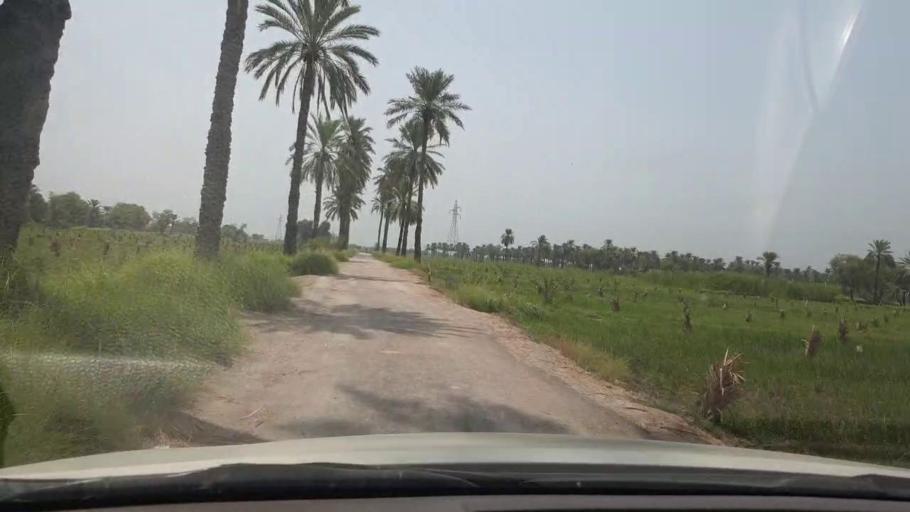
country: PK
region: Sindh
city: Shikarpur
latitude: 28.0206
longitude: 68.6169
